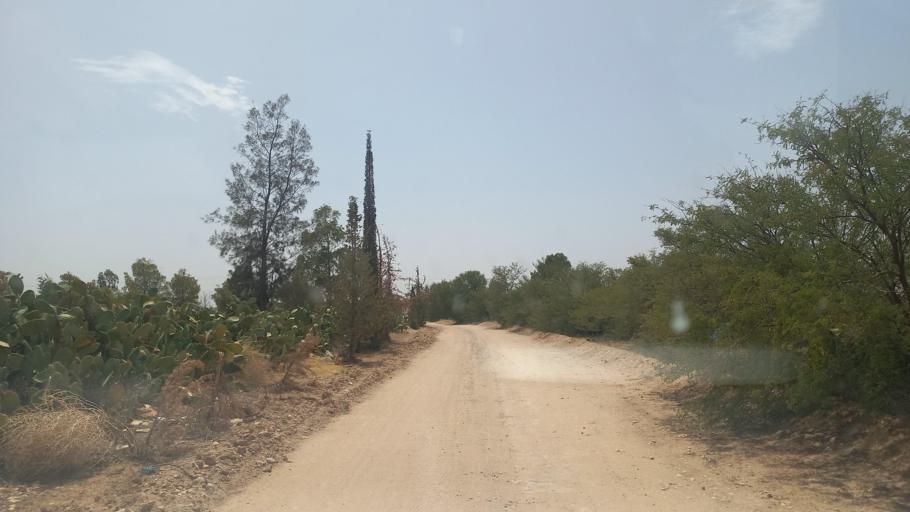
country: TN
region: Al Qasrayn
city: Kasserine
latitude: 35.2530
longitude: 9.0082
